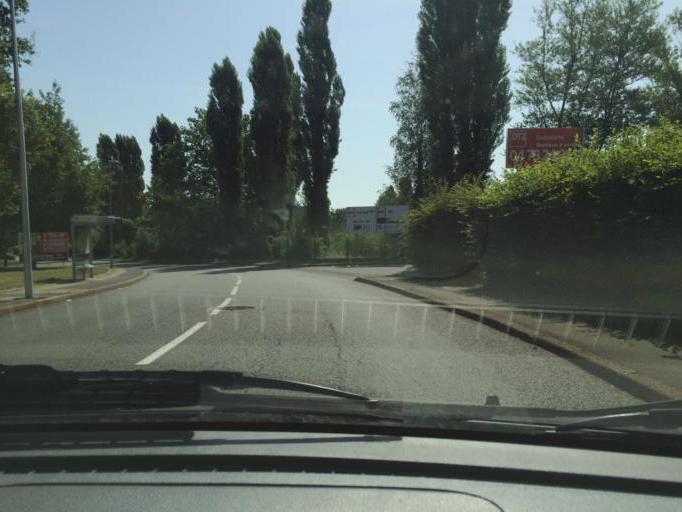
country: FR
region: Rhone-Alpes
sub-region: Departement du Rhone
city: Dardilly
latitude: 45.8054
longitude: 4.7742
